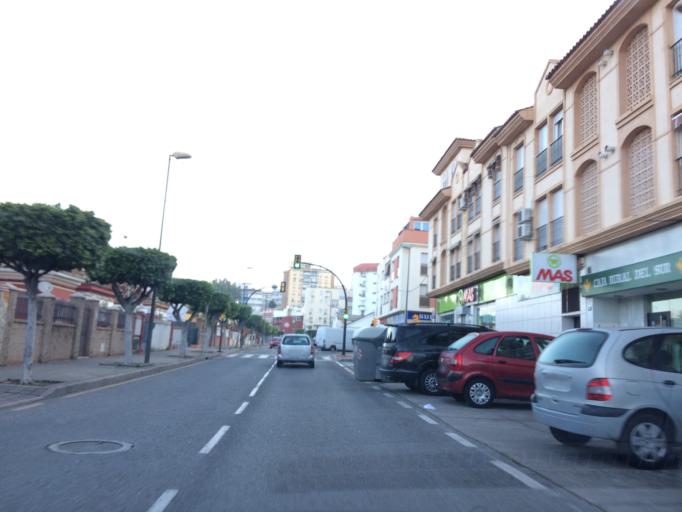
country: ES
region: Andalusia
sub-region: Provincia de Malaga
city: Malaga
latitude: 36.7471
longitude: -4.4217
